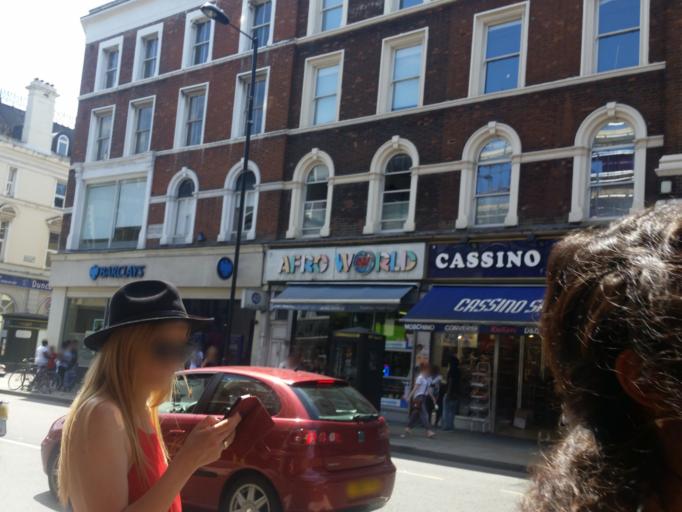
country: GB
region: England
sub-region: Greater London
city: Bethnal Green
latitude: 51.5466
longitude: -0.0757
